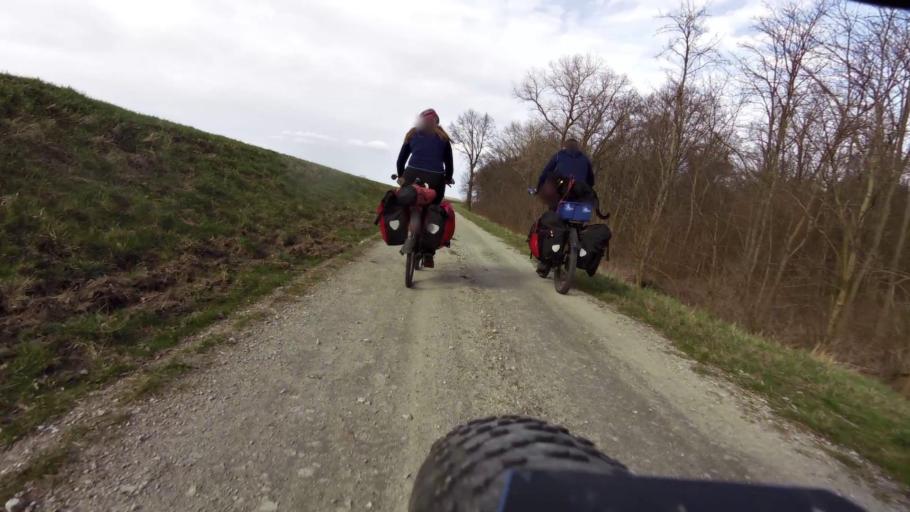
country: DE
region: Brandenburg
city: Reitwein
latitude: 52.5294
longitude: 14.6108
